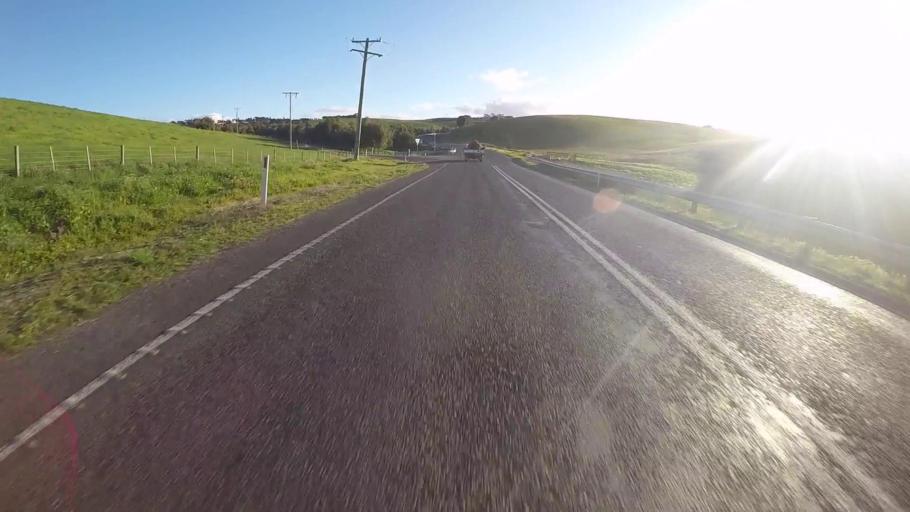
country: AU
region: Victoria
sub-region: Greater Geelong
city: Wandana Heights
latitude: -38.1705
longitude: 144.2389
